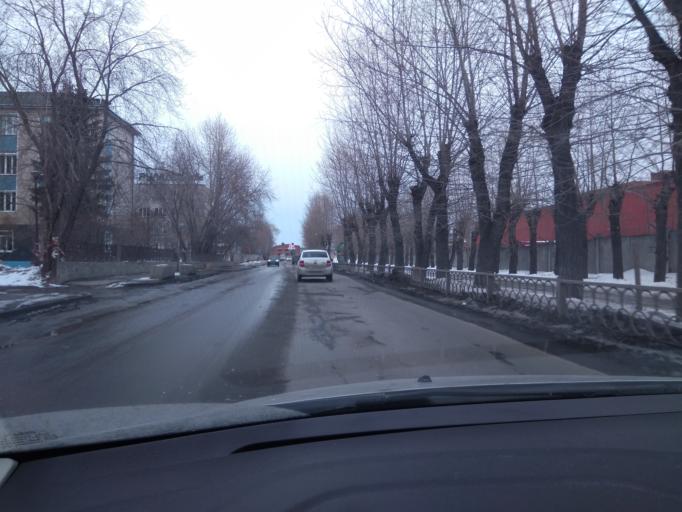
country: RU
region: Sverdlovsk
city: Yekaterinburg
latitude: 56.8758
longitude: 60.6143
